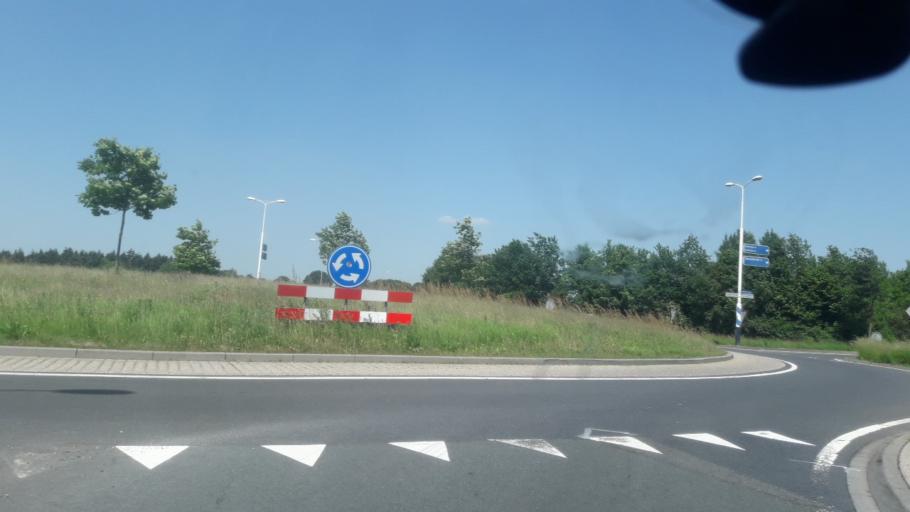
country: NL
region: Overijssel
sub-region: Gemeente Deventer
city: Schalkhaar
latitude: 52.2827
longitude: 6.2187
